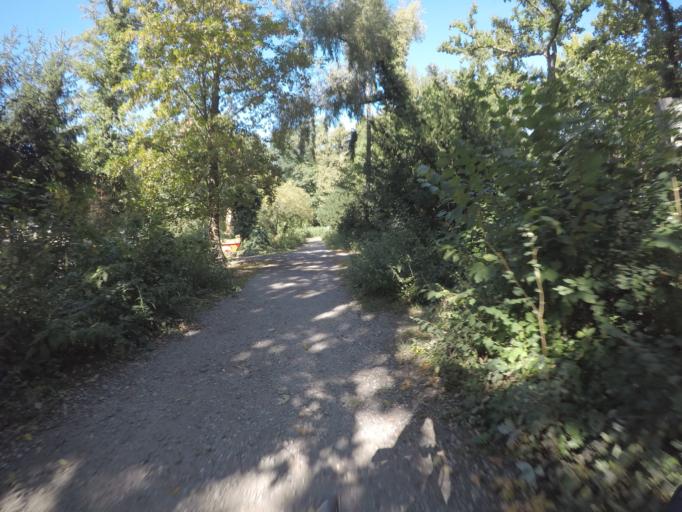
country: DE
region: Berlin
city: Tegel
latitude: 52.5917
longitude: 13.2693
